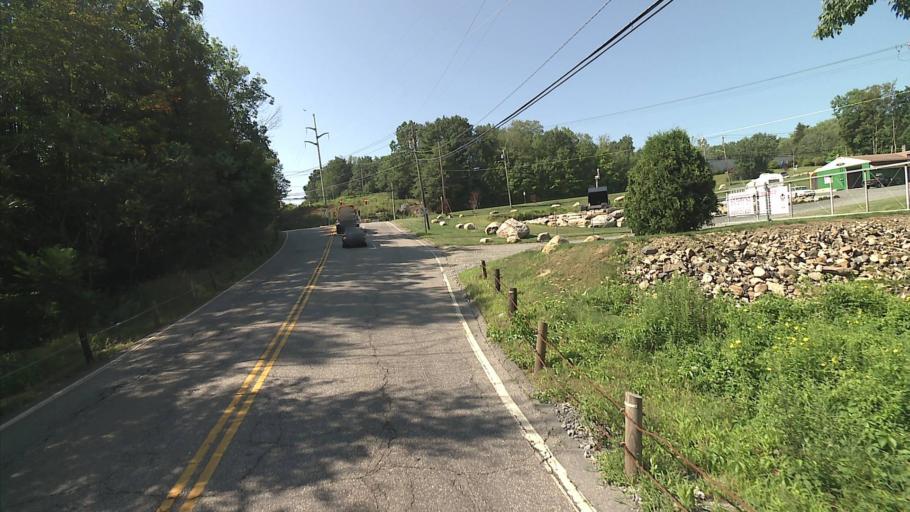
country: US
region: Connecticut
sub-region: Litchfield County
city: Northwest Harwinton
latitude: 41.8006
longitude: -73.0865
